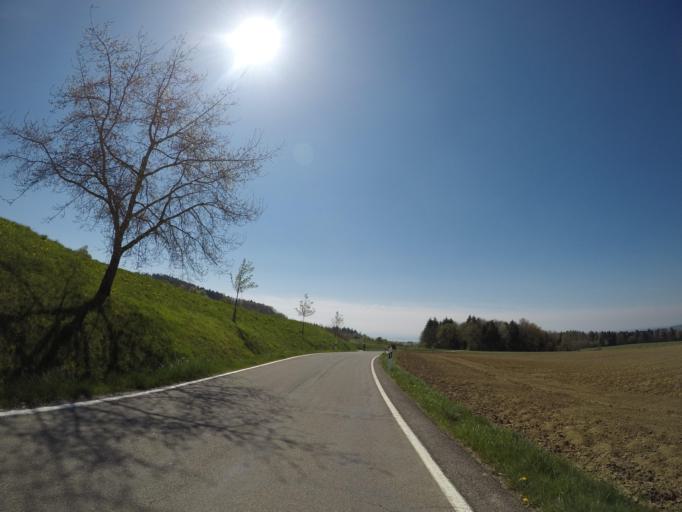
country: DE
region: Baden-Wuerttemberg
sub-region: Tuebingen Region
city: Markdorf
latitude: 47.7463
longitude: 9.3863
